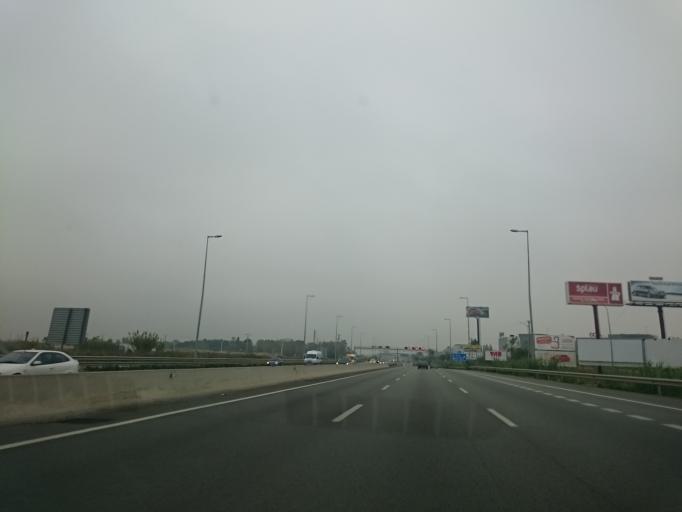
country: ES
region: Catalonia
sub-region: Provincia de Barcelona
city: El Prat de Llobregat
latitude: 41.3085
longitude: 2.0641
